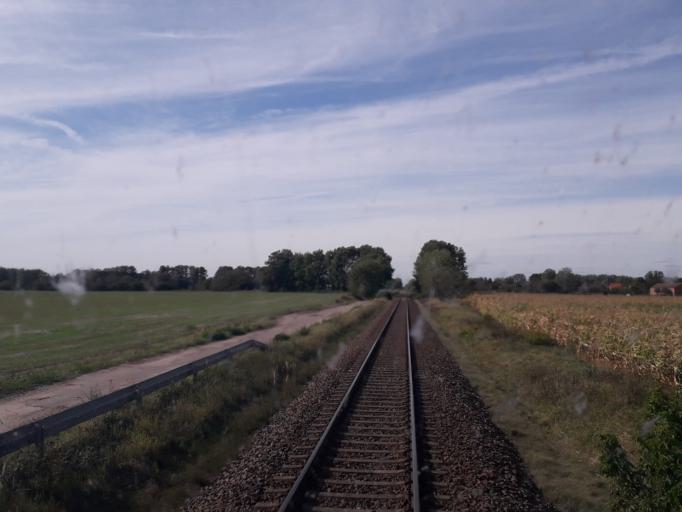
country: DE
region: Brandenburg
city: Kremmen
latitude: 52.8076
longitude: 13.0136
